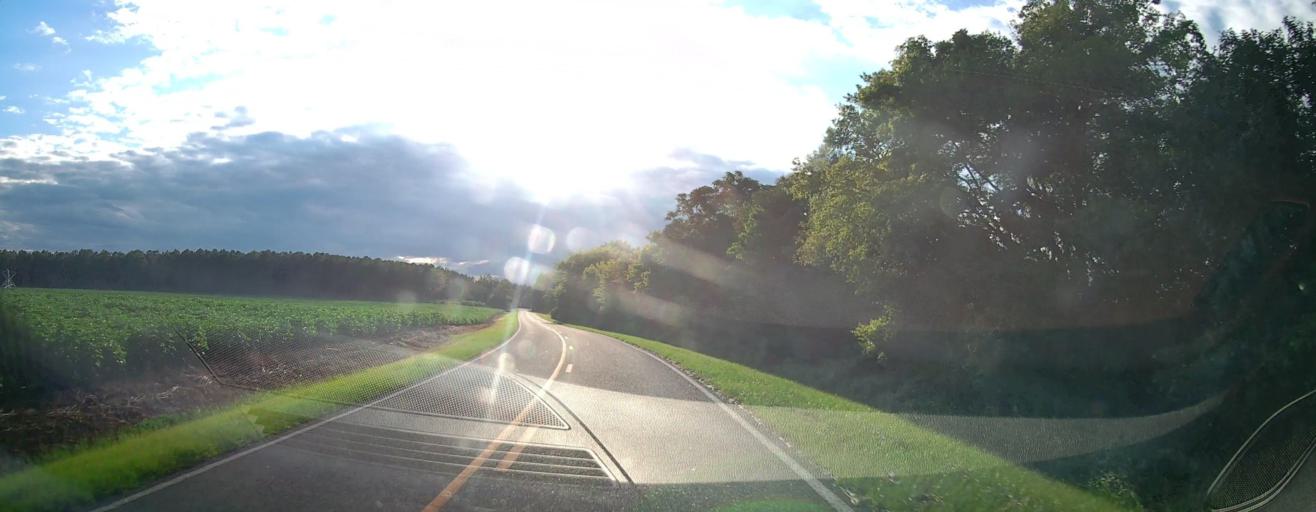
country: US
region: Georgia
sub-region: Pulaski County
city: Hawkinsville
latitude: 32.2875
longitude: -83.5459
